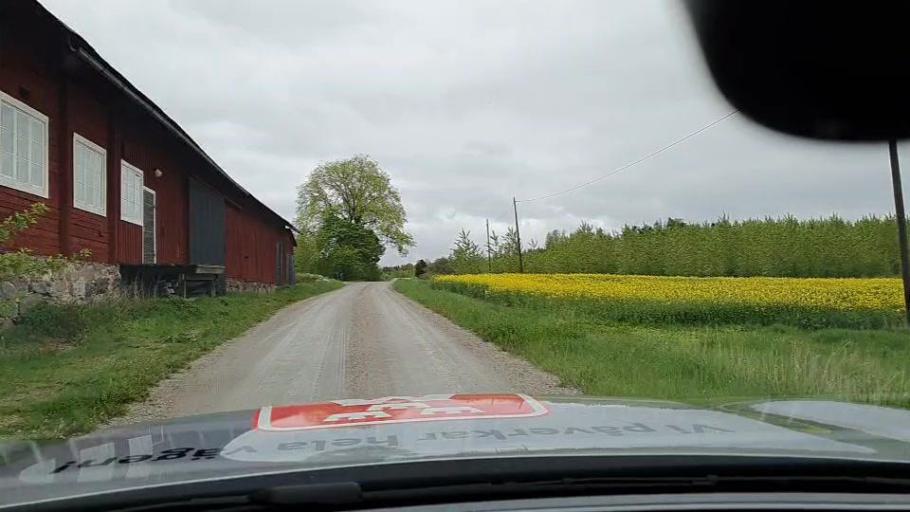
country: SE
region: Soedermanland
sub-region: Nykopings Kommun
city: Svalsta
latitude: 58.6401
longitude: 16.9333
